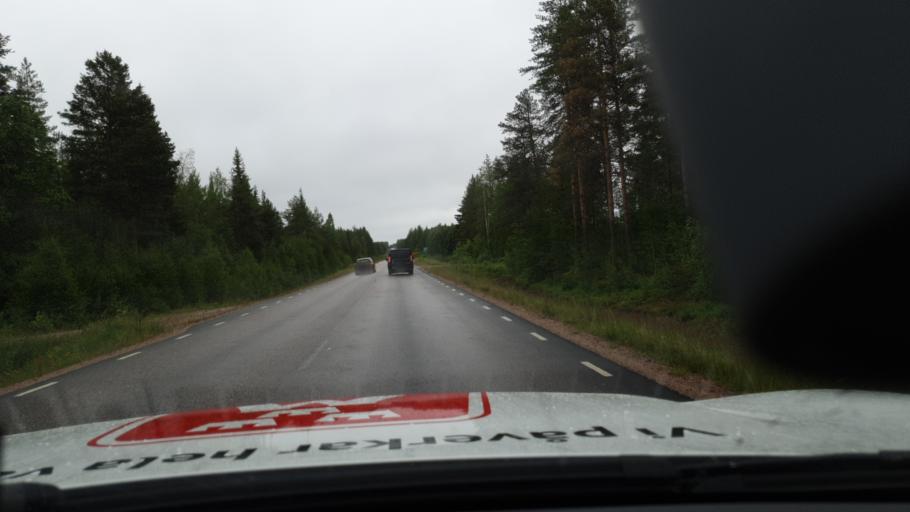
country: SE
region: Norrbotten
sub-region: Overtornea Kommun
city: OEvertornea
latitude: 66.5156
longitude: 23.7424
